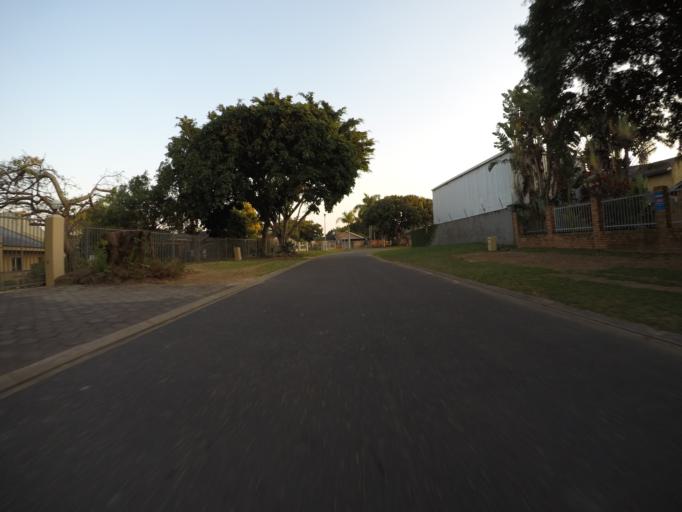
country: ZA
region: KwaZulu-Natal
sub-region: uThungulu District Municipality
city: Richards Bay
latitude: -28.7660
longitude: 32.1212
